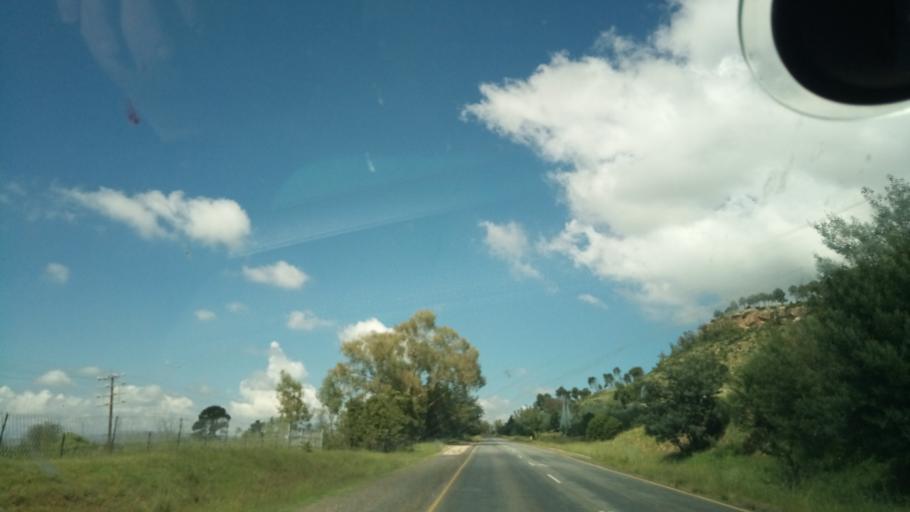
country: ZA
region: Orange Free State
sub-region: Thabo Mofutsanyana District Municipality
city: Ficksburg
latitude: -28.8570
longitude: 27.8775
